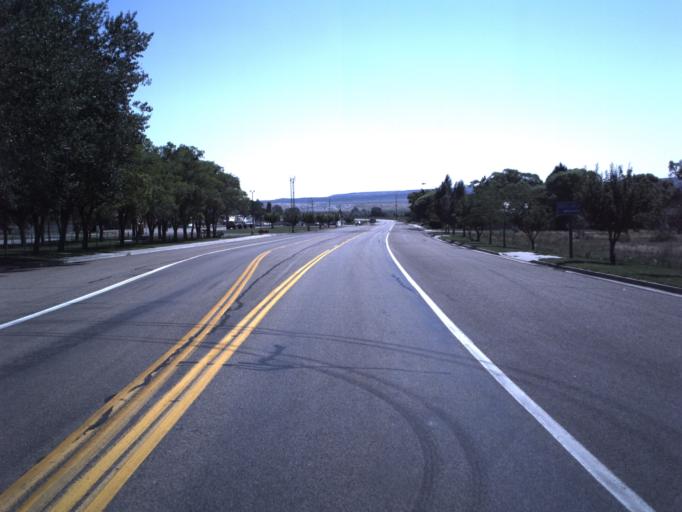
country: US
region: Utah
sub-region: Emery County
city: Ferron
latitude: 38.9231
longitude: -111.2523
